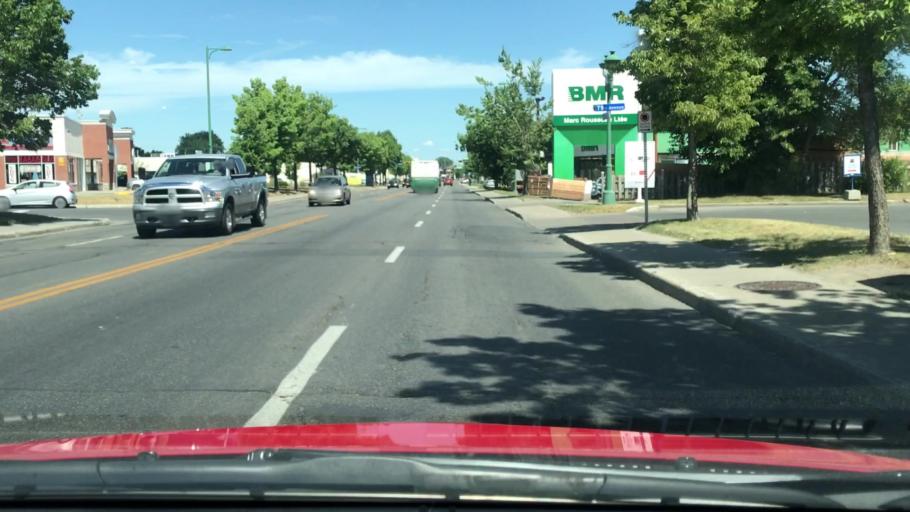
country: CA
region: Quebec
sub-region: Laval
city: Laval
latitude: 45.5373
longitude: -73.7403
